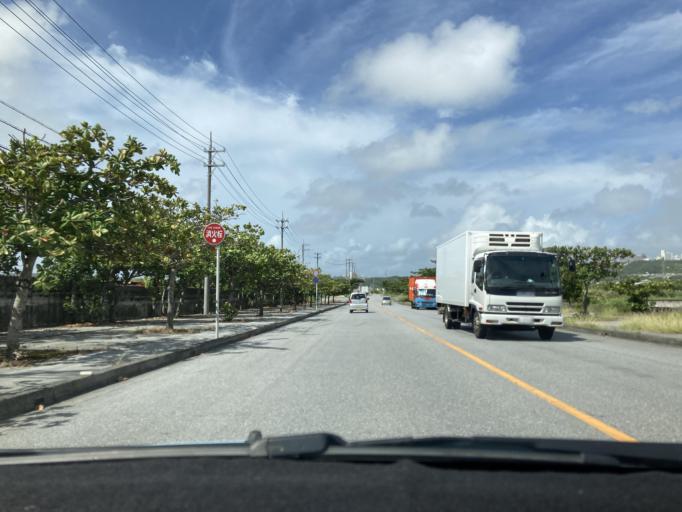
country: JP
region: Okinawa
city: Ginowan
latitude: 26.2198
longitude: 127.7768
